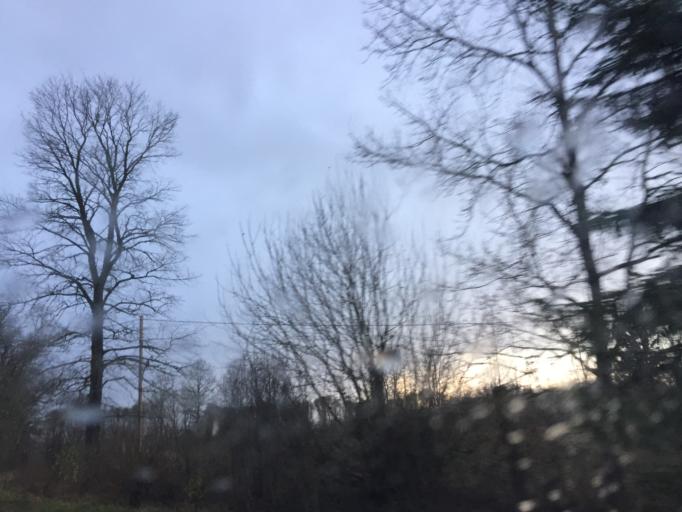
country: LV
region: Burtnieki
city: Matisi
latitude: 57.6969
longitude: 25.2671
